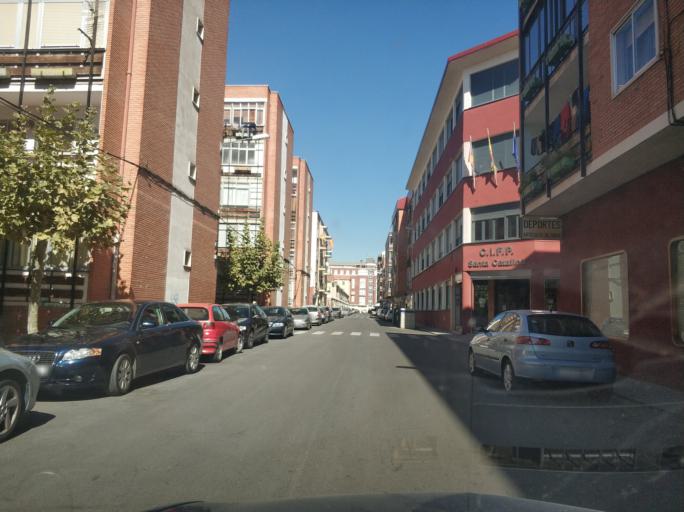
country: ES
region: Castille and Leon
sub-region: Provincia de Burgos
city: Aranda de Duero
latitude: 41.6707
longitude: -3.6770
